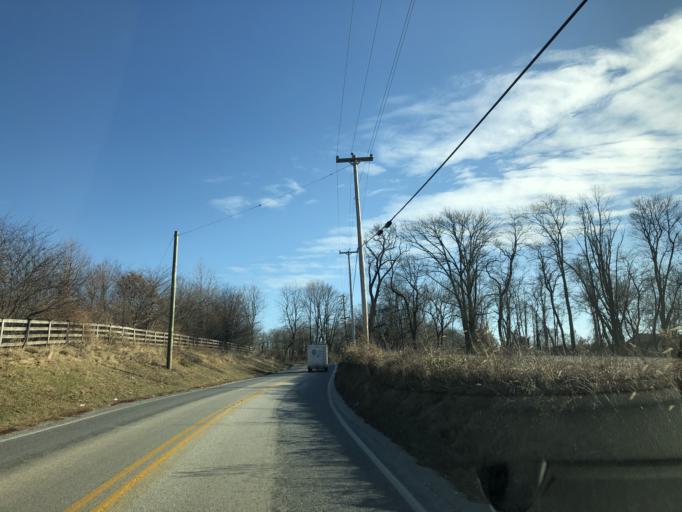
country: US
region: Pennsylvania
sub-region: Chester County
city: Toughkenamon
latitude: 39.8515
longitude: -75.7689
